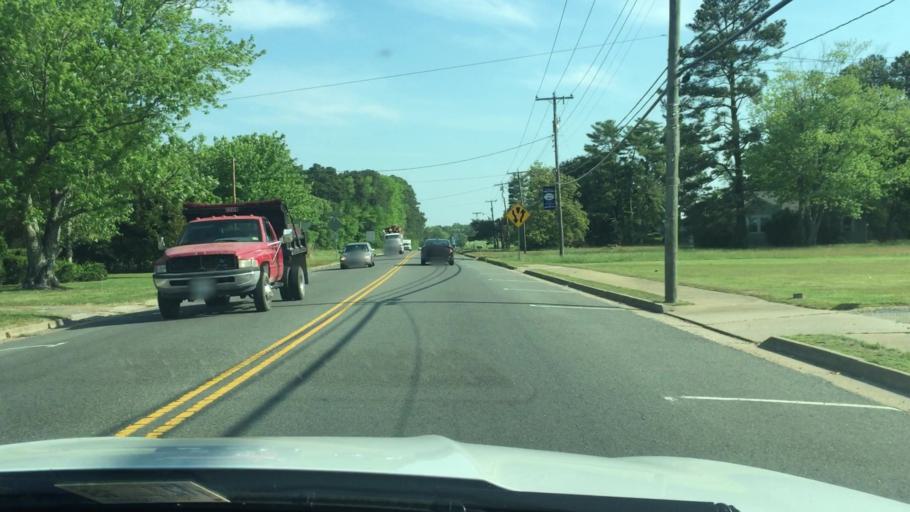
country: US
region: Virginia
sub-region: Lancaster County
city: Kilmarnock
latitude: 37.6501
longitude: -76.3887
